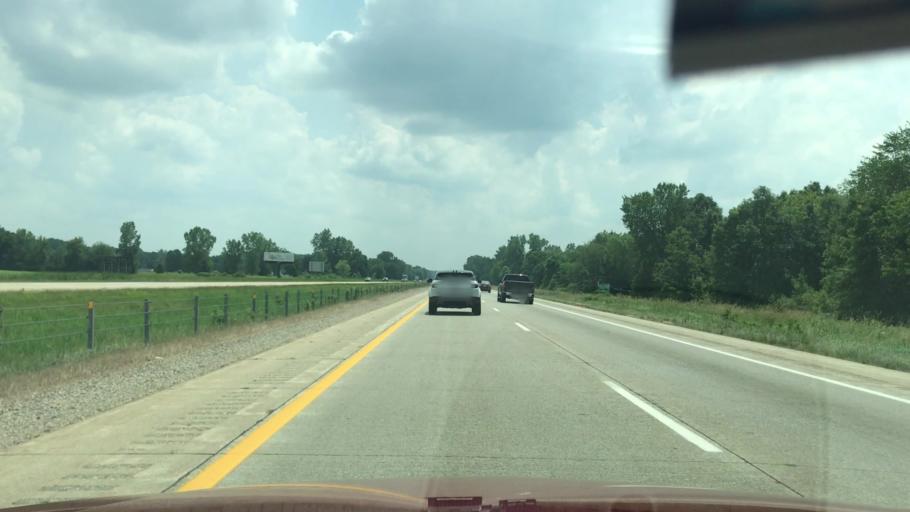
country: US
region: Michigan
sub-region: Allegan County
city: Plainwell
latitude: 42.4278
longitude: -85.6609
